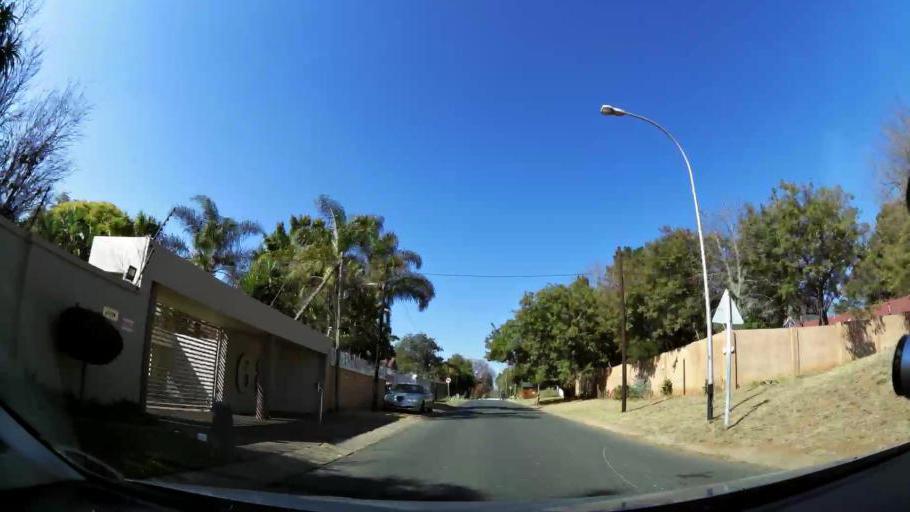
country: ZA
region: Gauteng
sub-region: City of Johannesburg Metropolitan Municipality
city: Modderfontein
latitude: -26.1347
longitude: 28.1122
